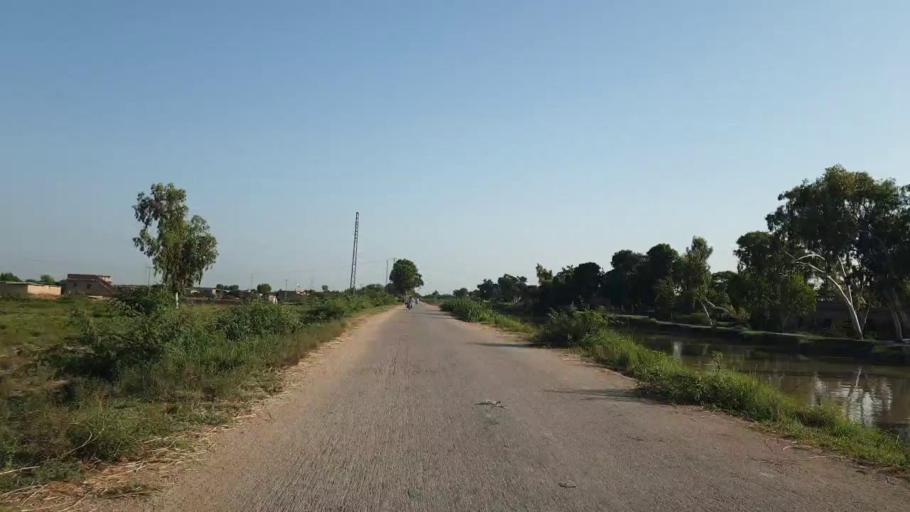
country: PK
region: Sindh
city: Hyderabad
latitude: 25.3099
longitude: 68.4324
